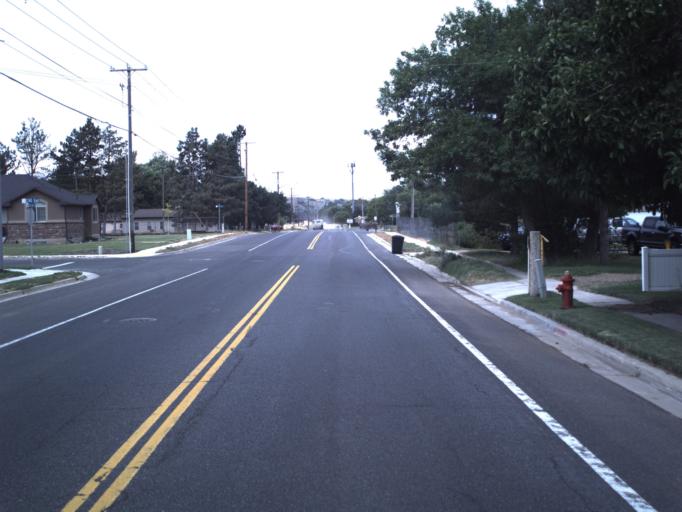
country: US
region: Utah
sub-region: Davis County
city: South Weber
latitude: 41.1325
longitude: -111.9335
